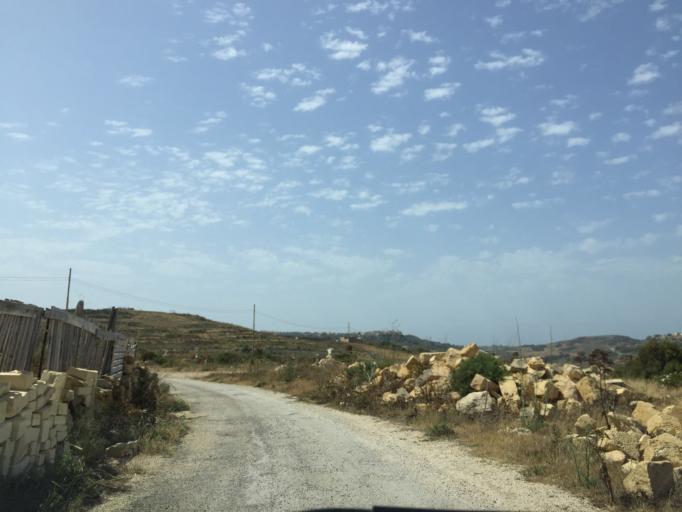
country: MT
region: In-Nadur
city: Nadur
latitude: 36.0626
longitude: 14.2893
